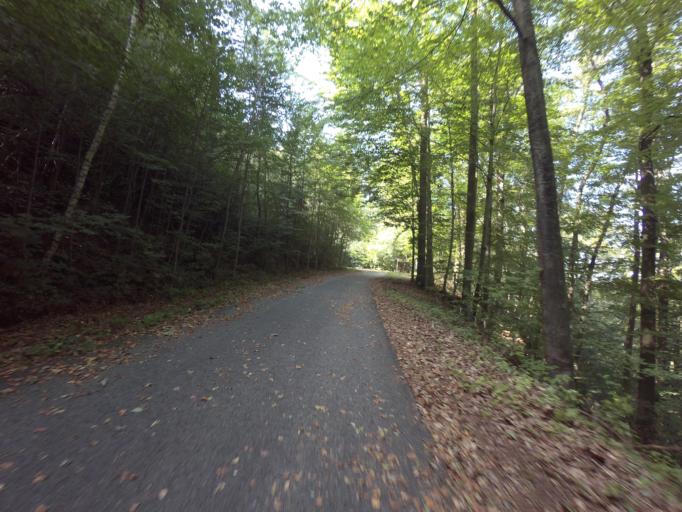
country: CZ
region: Jihocesky
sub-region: Okres Ceske Budejovice
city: Hluboka nad Vltavou
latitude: 49.0905
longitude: 14.4627
